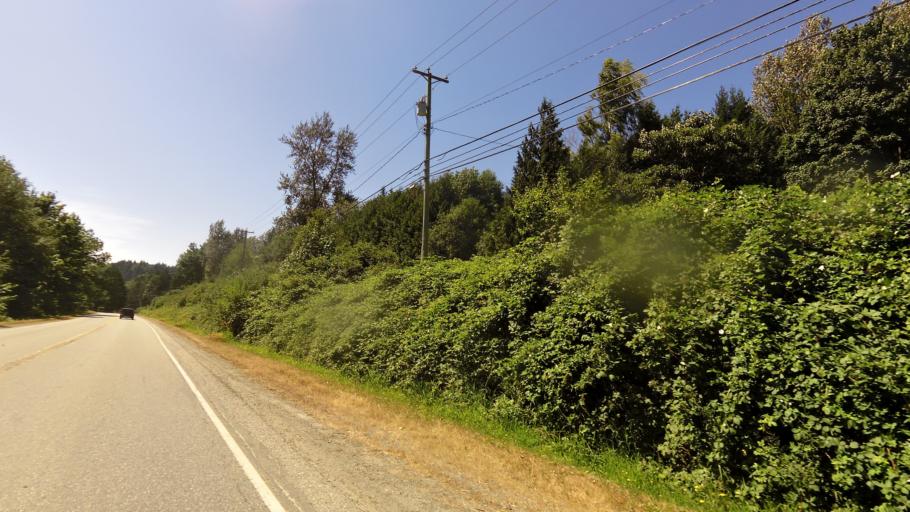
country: CA
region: British Columbia
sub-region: Fraser Valley Regional District
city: Chilliwack
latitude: 49.1945
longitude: -122.0633
